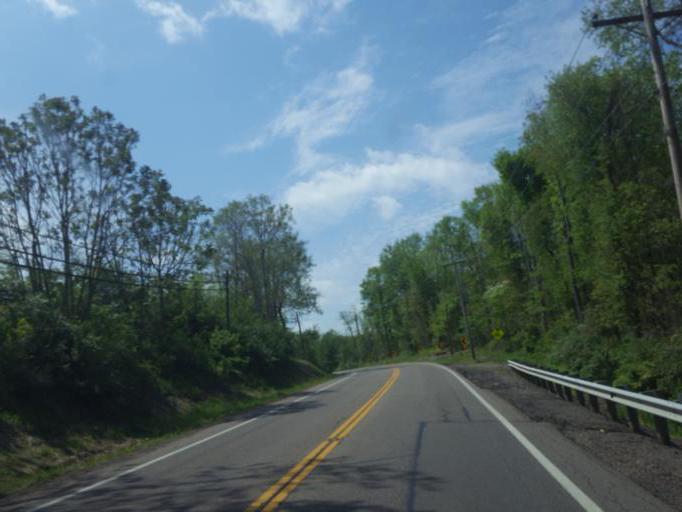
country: US
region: Ohio
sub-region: Licking County
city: Newark
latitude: 40.0282
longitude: -82.4020
